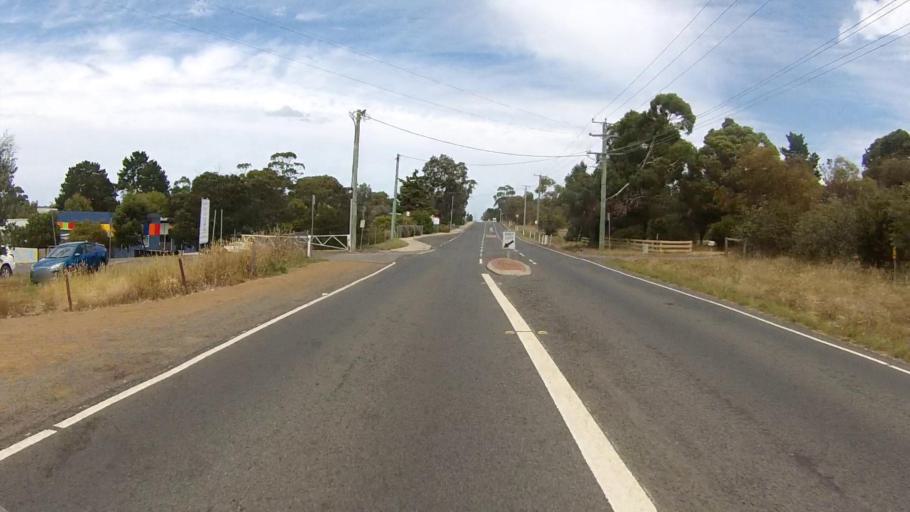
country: AU
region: Tasmania
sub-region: Clarence
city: Lauderdale
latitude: -42.9023
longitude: 147.4784
